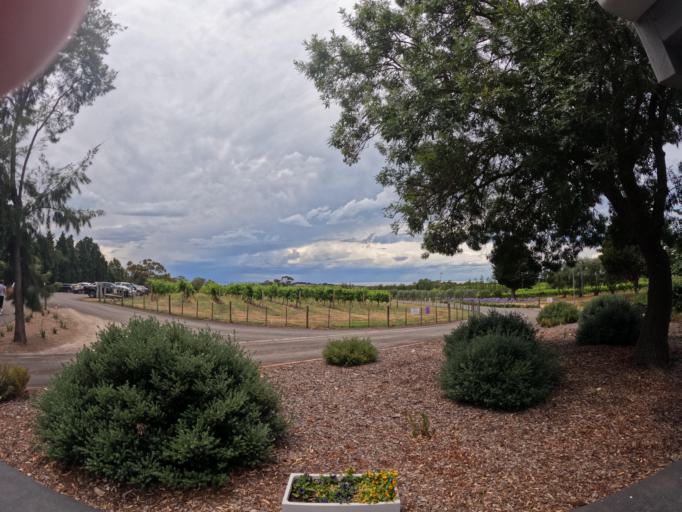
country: AU
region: Victoria
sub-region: Greater Geelong
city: Clifton Springs
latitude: -38.1521
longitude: 144.6193
